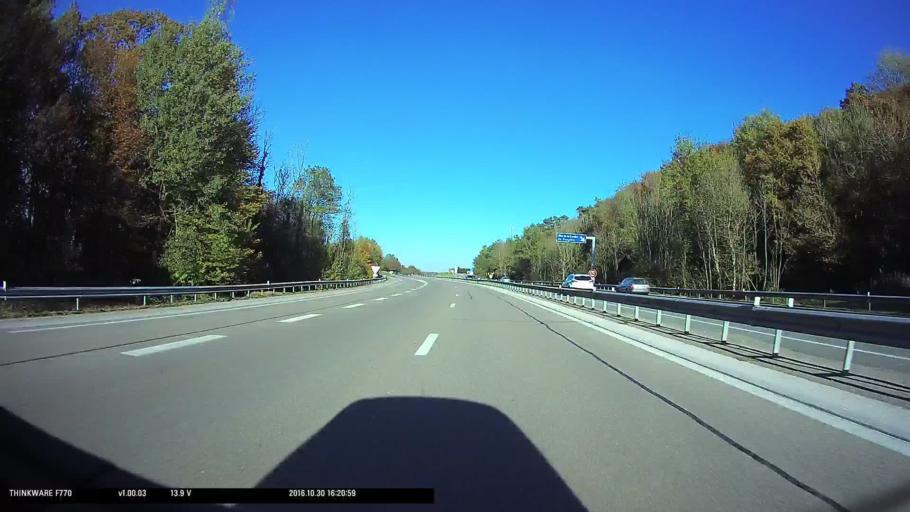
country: FR
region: Franche-Comte
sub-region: Departement du Doubs
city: Clerval
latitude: 47.4025
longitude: 6.4413
